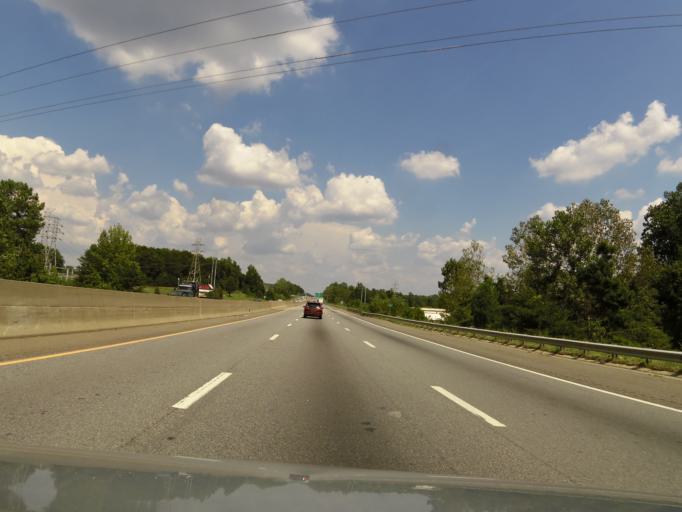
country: US
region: North Carolina
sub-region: Gaston County
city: Bessemer City
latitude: 35.2680
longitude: -81.2526
